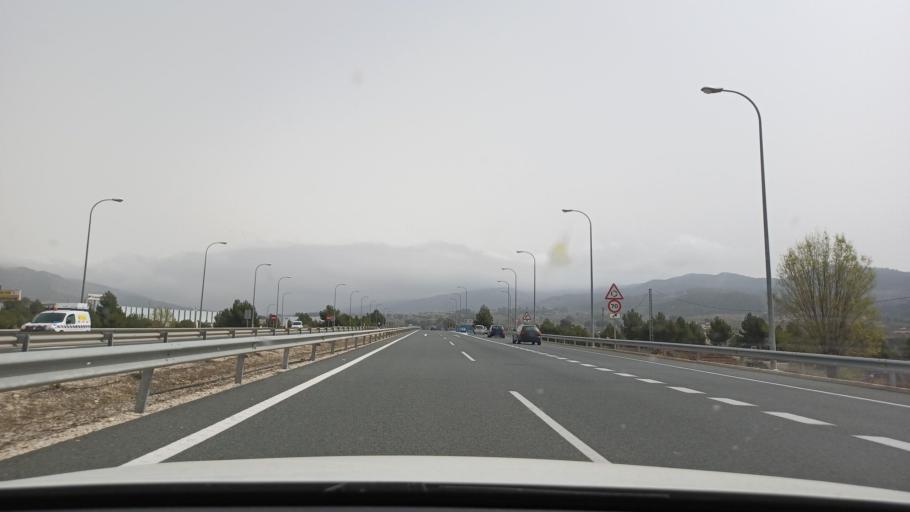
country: ES
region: Valencia
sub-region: Provincia de Alicante
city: Ibi
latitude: 38.6062
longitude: -0.5949
